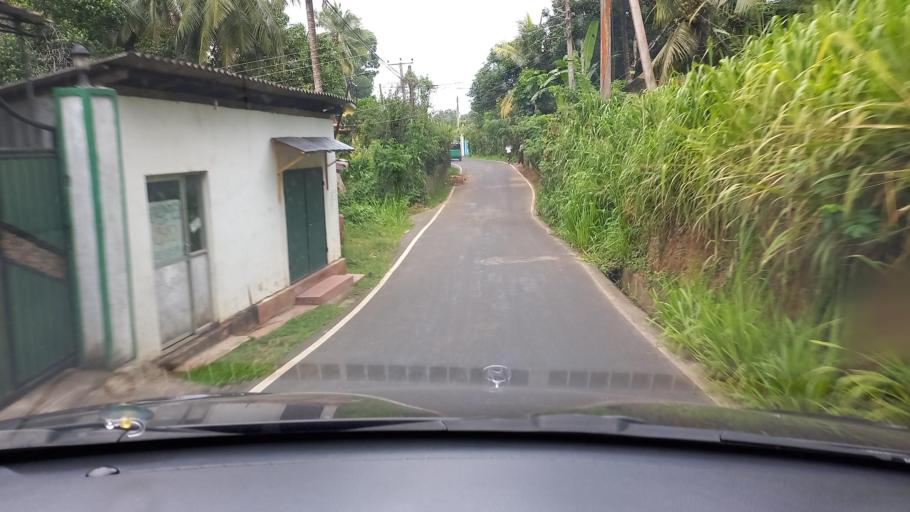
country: LK
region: Central
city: Kadugannawa
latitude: 7.2594
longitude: 80.3521
